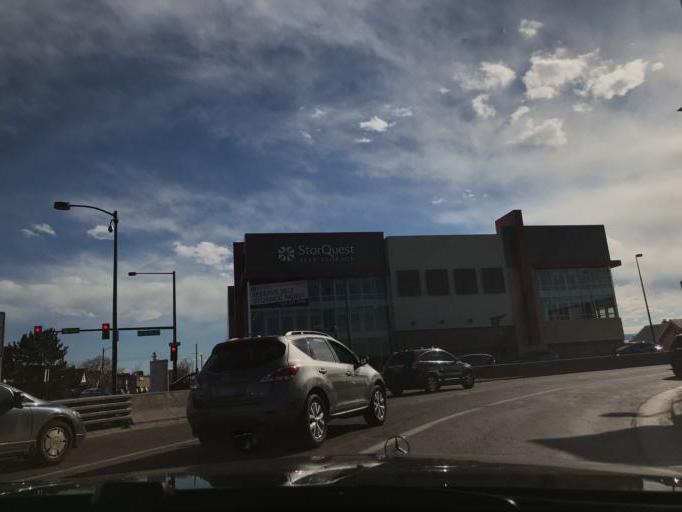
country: US
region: Colorado
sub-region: Denver County
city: Denver
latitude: 39.7261
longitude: -105.0003
